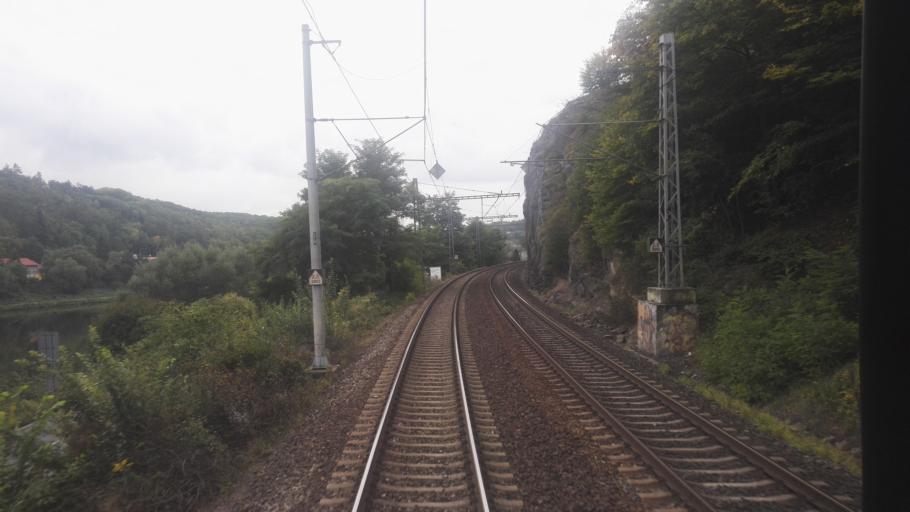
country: CZ
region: Central Bohemia
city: Roztoky
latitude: 50.1424
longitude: 14.3961
